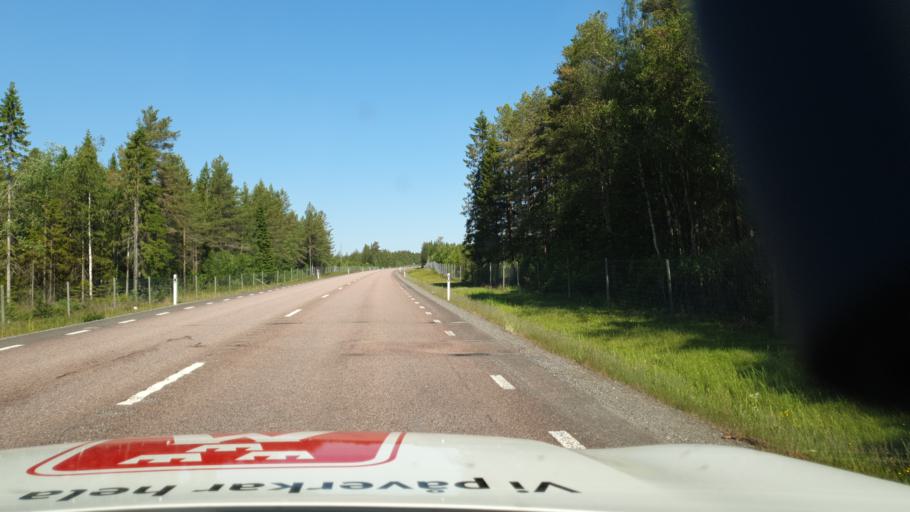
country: SE
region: Vaesterbotten
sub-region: Skelleftea Kommun
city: Burea
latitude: 64.4152
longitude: 21.2910
